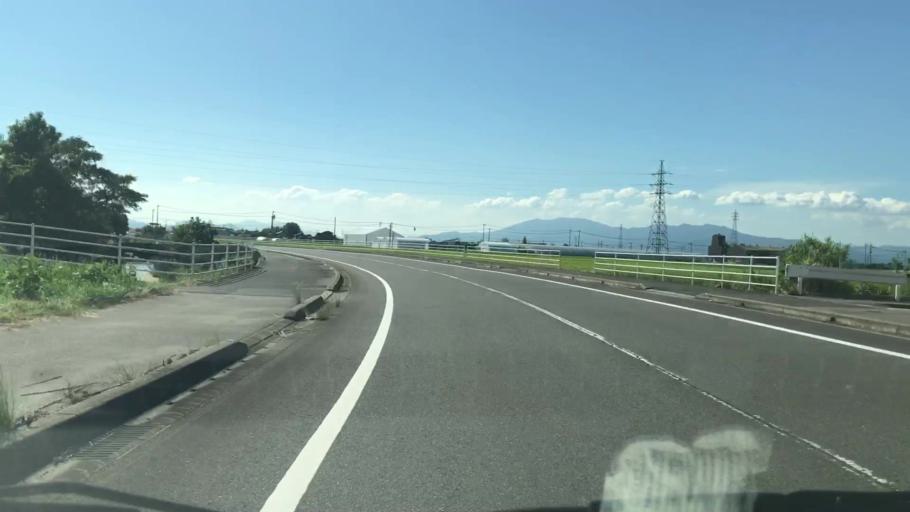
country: JP
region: Saga Prefecture
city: Okawa
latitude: 33.2303
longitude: 130.3665
